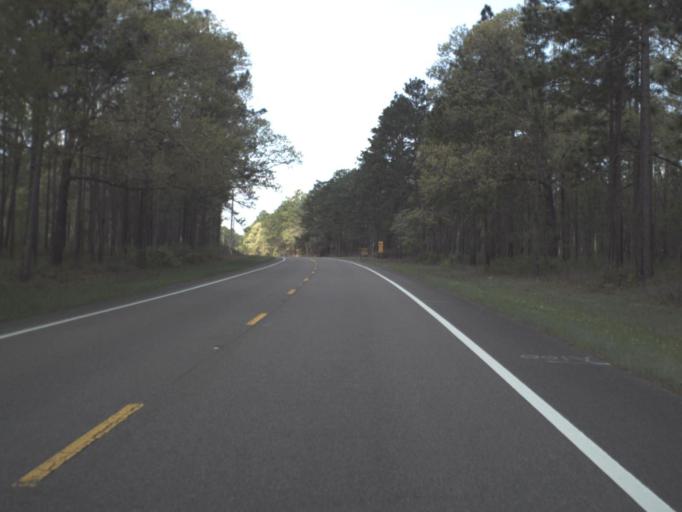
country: US
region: Florida
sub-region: Santa Rosa County
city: Point Baker
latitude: 30.8548
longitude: -86.8363
